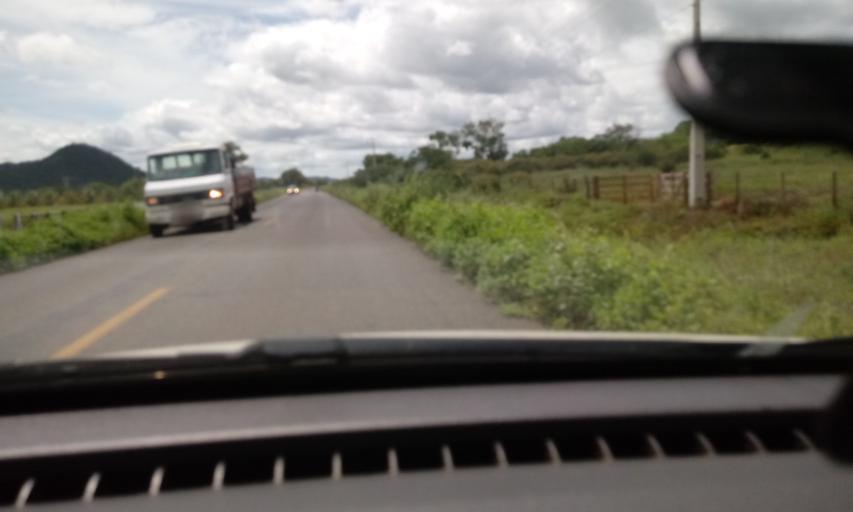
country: BR
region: Bahia
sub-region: Guanambi
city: Guanambi
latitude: -14.1326
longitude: -42.8500
